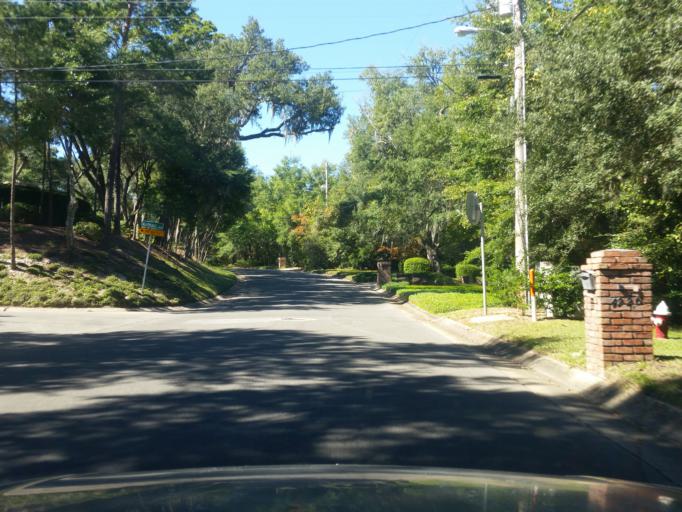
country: US
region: Florida
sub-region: Escambia County
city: East Pensacola Heights
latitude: 30.4726
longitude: -87.1650
